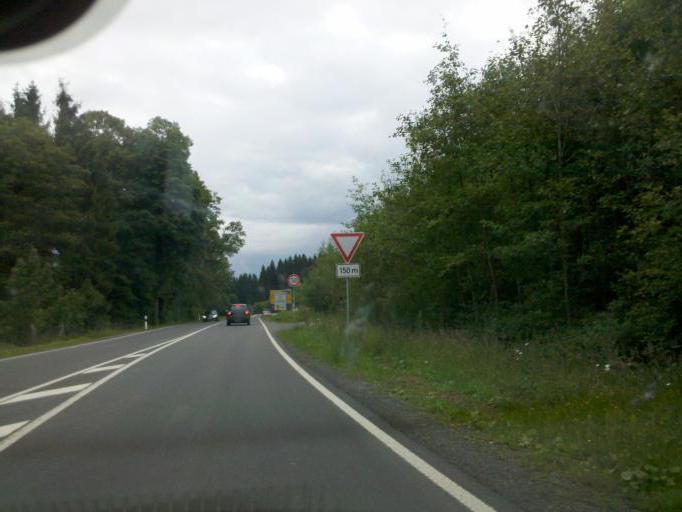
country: DE
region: North Rhine-Westphalia
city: Kreuztal
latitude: 51.0115
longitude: 7.9416
